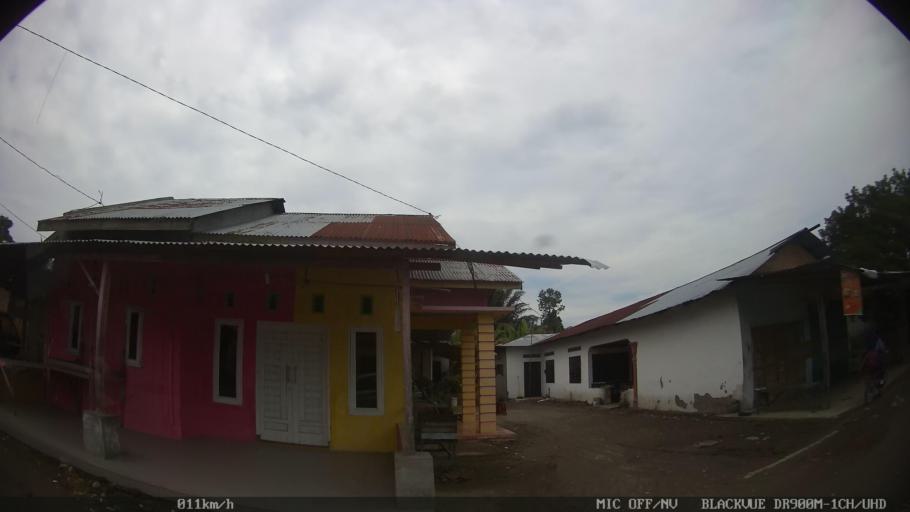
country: ID
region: North Sumatra
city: Sunggal
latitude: 3.6308
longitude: 98.5619
